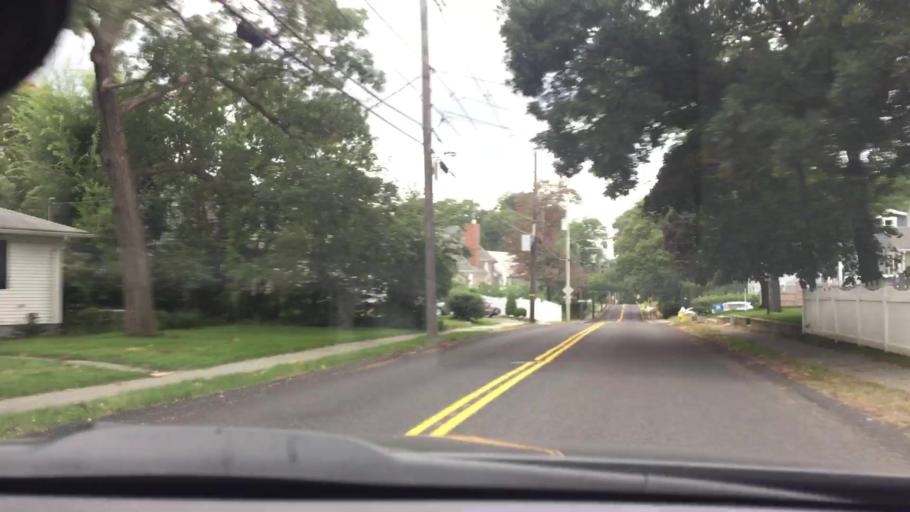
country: US
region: Massachusetts
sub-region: Norfolk County
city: Needham
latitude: 42.2886
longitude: -71.2195
